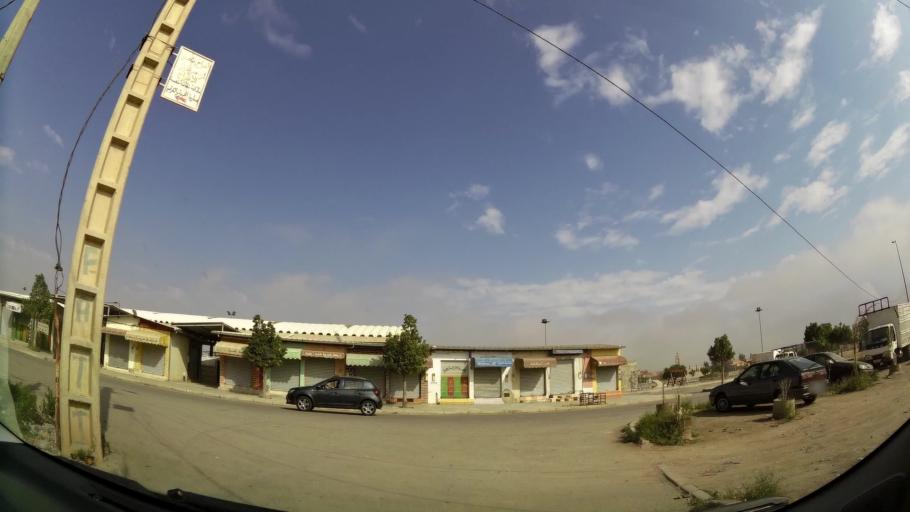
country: MA
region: Oriental
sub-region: Oujda-Angad
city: Oujda
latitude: 34.6890
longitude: -1.8994
